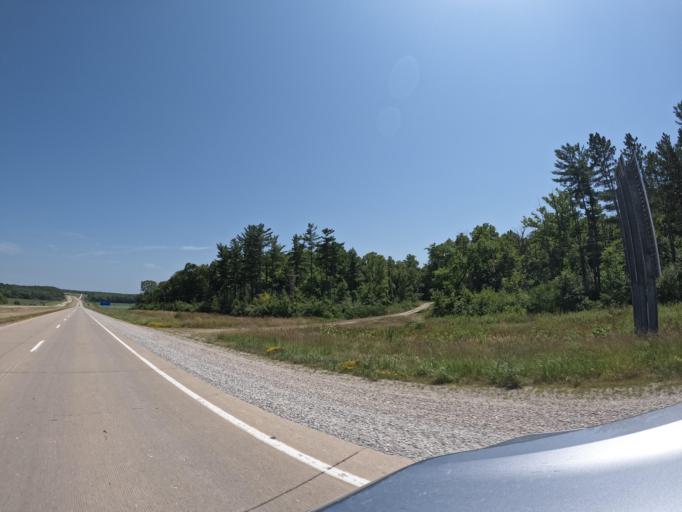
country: US
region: Iowa
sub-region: Henry County
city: Mount Pleasant
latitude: 40.9736
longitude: -91.6562
